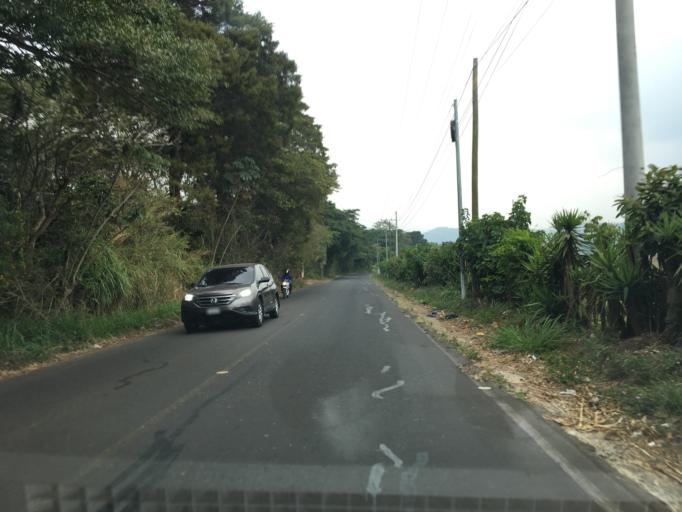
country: GT
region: Guatemala
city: Fraijanes
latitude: 14.3781
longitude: -90.4896
